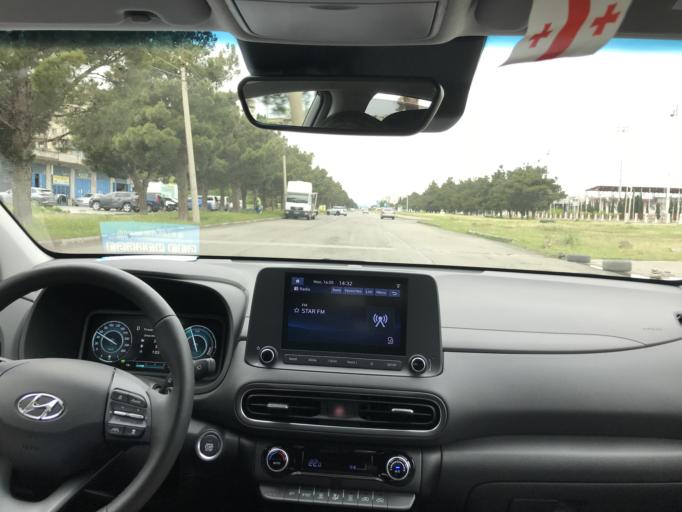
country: GE
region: Kvemo Kartli
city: Rust'avi
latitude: 41.5696
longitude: 44.9952
